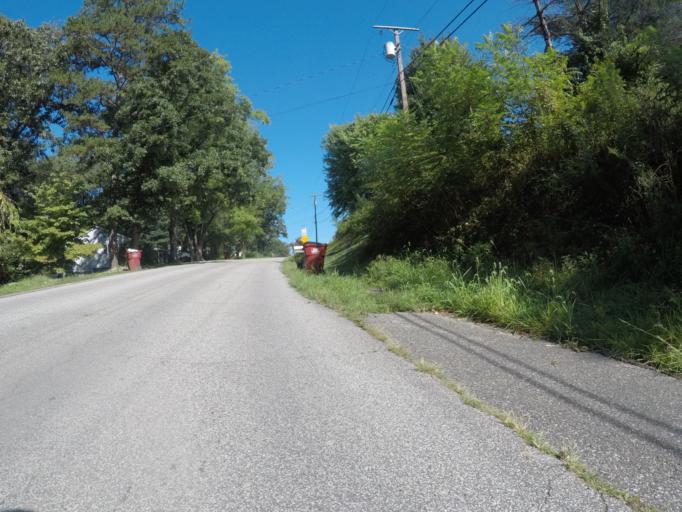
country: US
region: Kentucky
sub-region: Boyd County
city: Westwood
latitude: 38.4846
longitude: -82.6867
